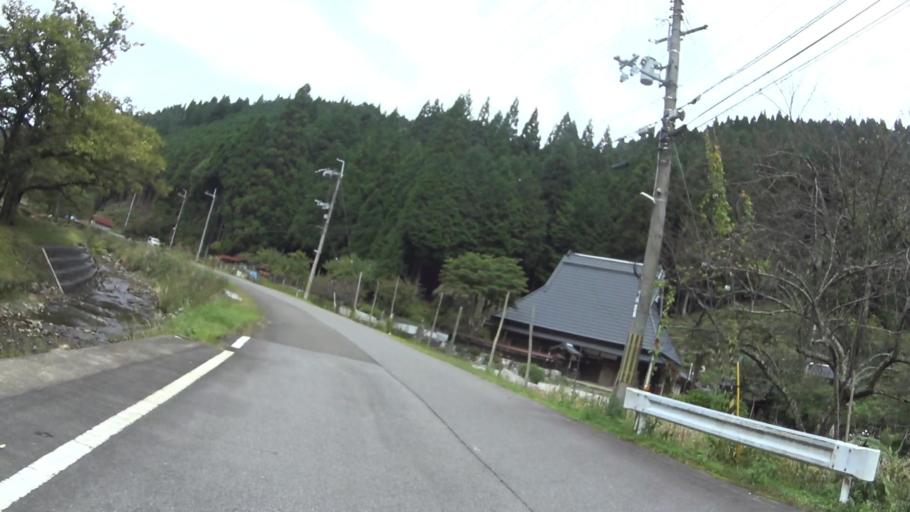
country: JP
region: Shiga Prefecture
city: Kitahama
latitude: 35.2608
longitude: 135.7525
